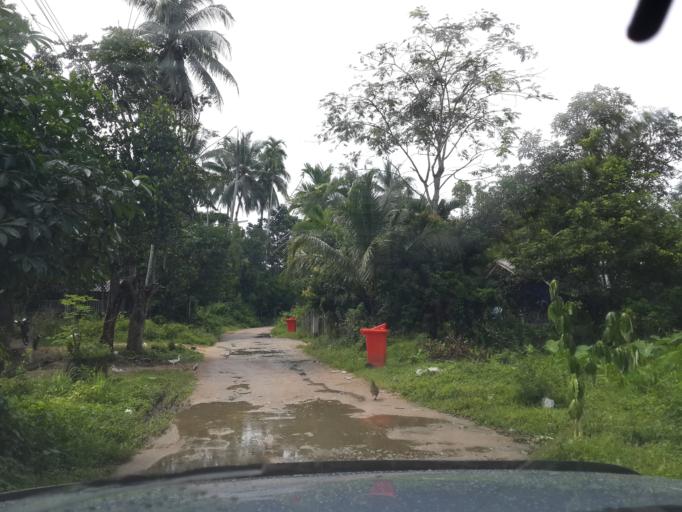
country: TH
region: Narathiwat
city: Rueso
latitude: 6.3834
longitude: 101.5201
